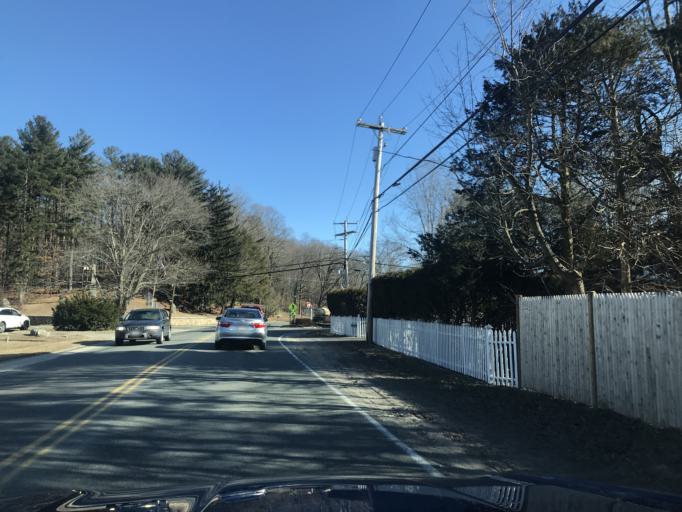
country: US
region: Massachusetts
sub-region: Essex County
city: Groveland
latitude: 42.7074
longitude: -71.0652
